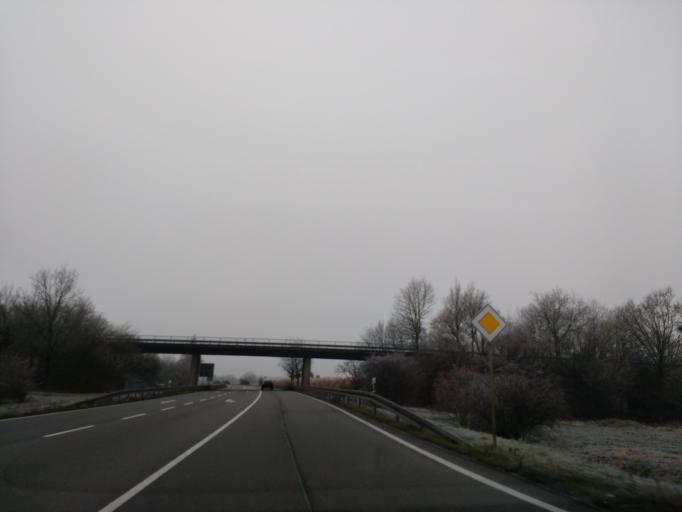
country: DE
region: Baden-Wuerttemberg
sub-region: Freiburg Region
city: Appenweier
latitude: 48.5403
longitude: 8.0203
